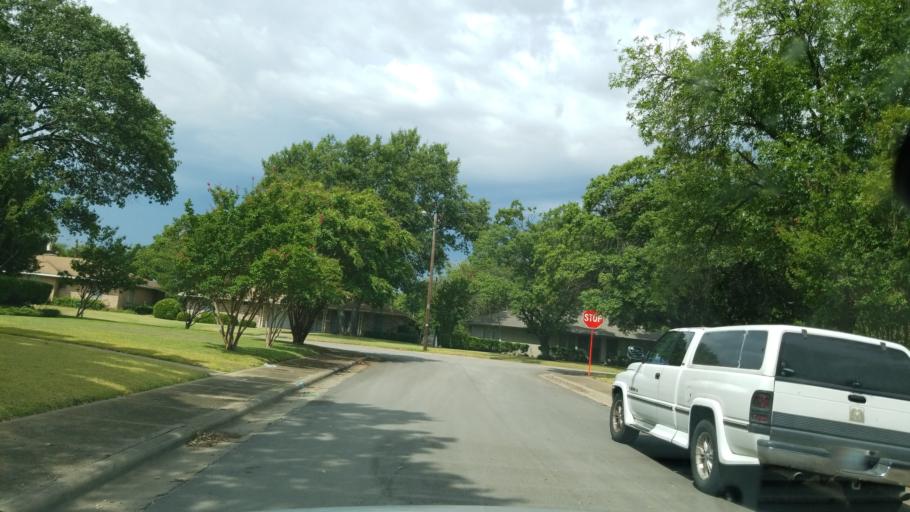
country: US
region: Texas
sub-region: Dallas County
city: Duncanville
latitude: 32.6728
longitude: -96.8546
